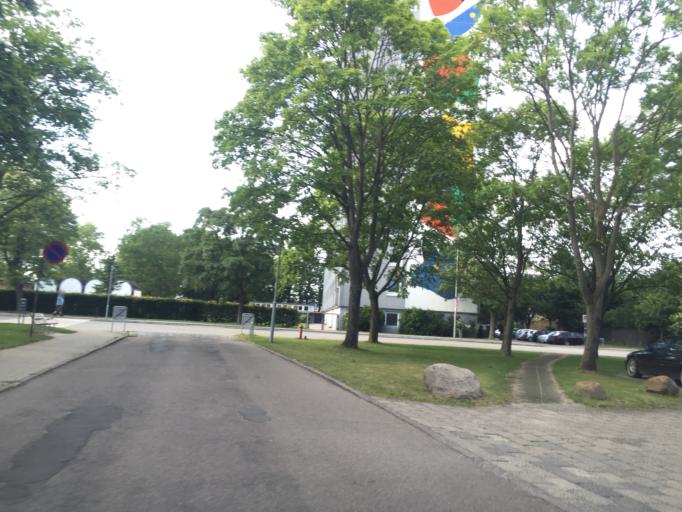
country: DK
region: Capital Region
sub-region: Rodovre Kommune
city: Rodovre
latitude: 55.6684
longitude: 12.4451
